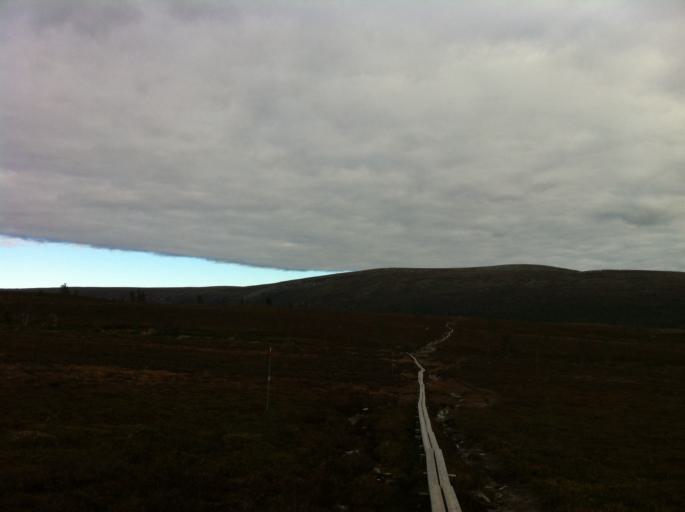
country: NO
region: Hedmark
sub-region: Engerdal
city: Engerdal
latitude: 62.0999
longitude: 12.2705
